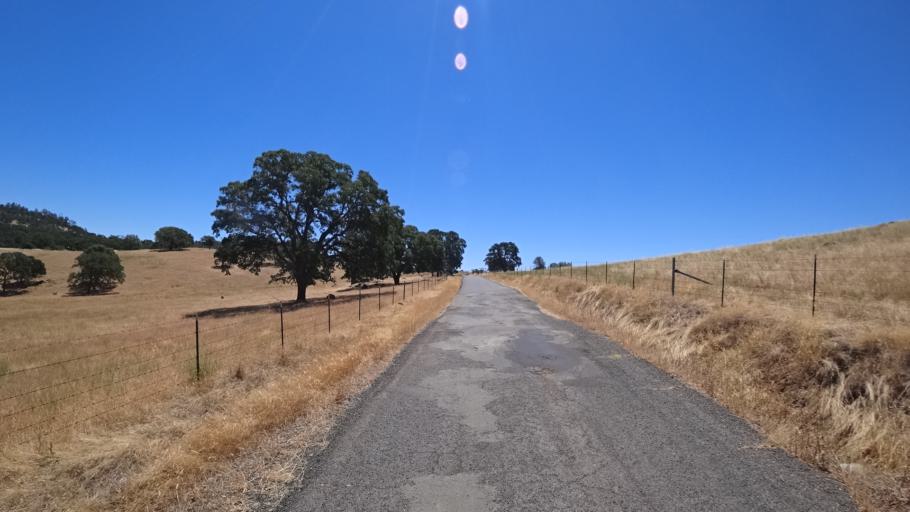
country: US
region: California
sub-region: Calaveras County
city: Rancho Calaveras
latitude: 38.0506
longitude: -120.8009
